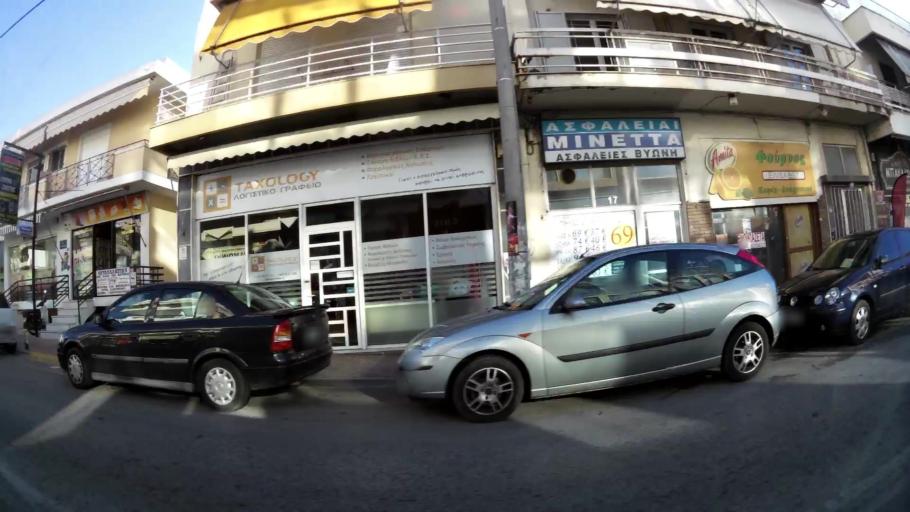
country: GR
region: Attica
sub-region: Nomarchia Anatolikis Attikis
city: Pallini
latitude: 38.0027
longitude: 23.8808
